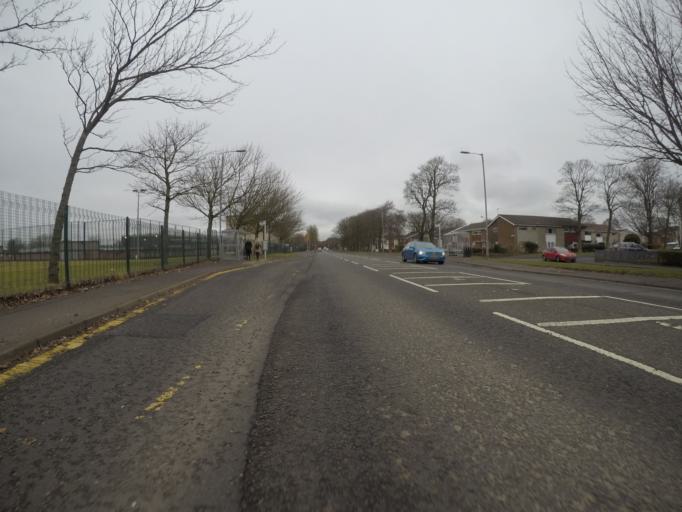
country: GB
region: Scotland
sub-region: North Ayrshire
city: Irvine
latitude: 55.6268
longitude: -4.6738
